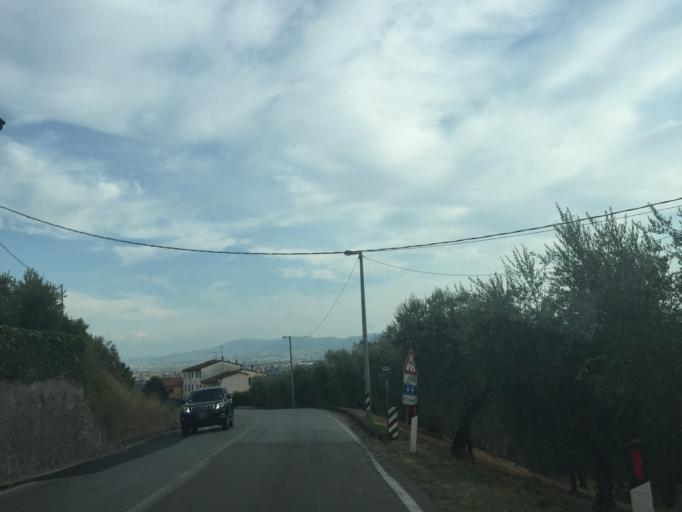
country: IT
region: Tuscany
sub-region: Provincia di Pistoia
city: Pistoia
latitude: 43.9743
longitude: 10.8817
